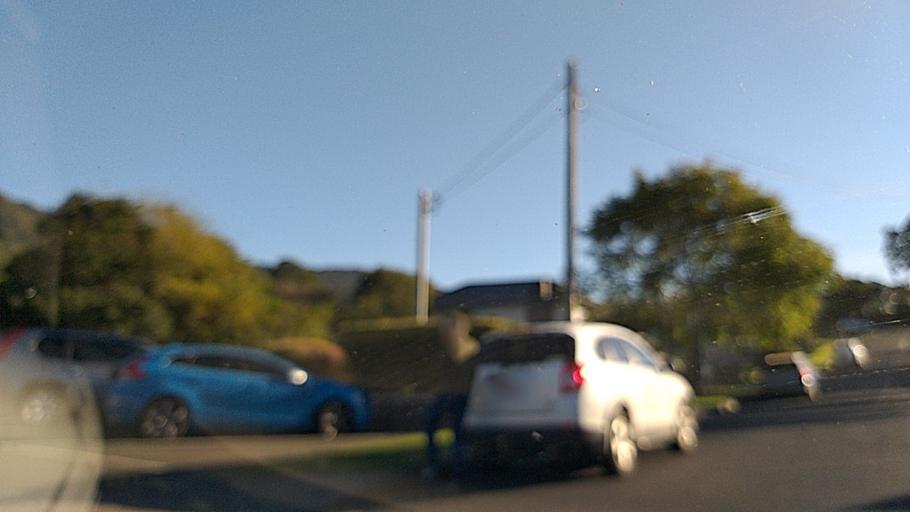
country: AU
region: New South Wales
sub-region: Wollongong
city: Bulli
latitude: -34.3413
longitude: 150.9054
